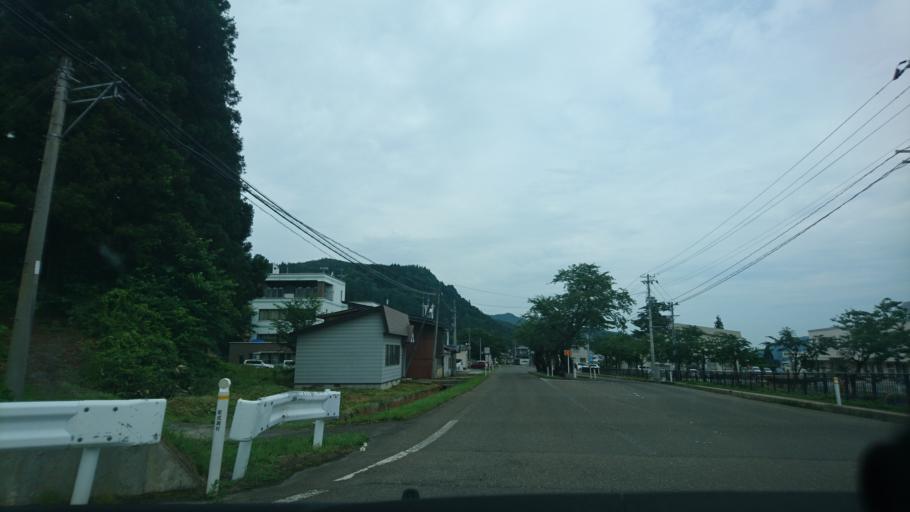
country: JP
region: Akita
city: Yuzawa
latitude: 39.1796
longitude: 140.6506
